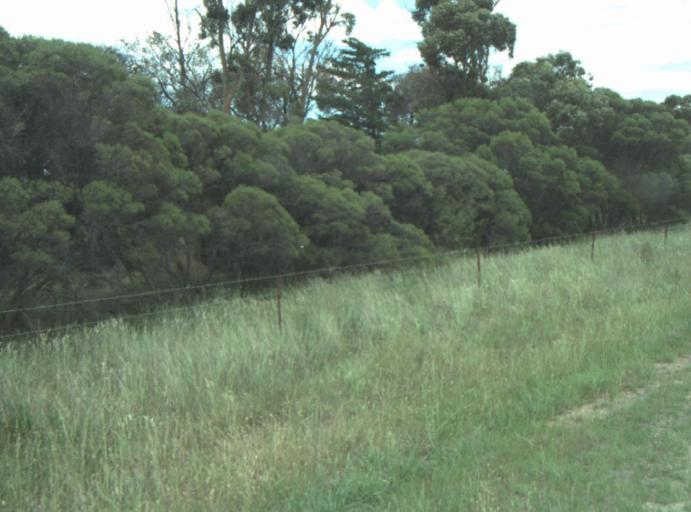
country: AU
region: Victoria
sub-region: Wyndham
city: Little River
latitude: -37.9262
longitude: 144.4644
